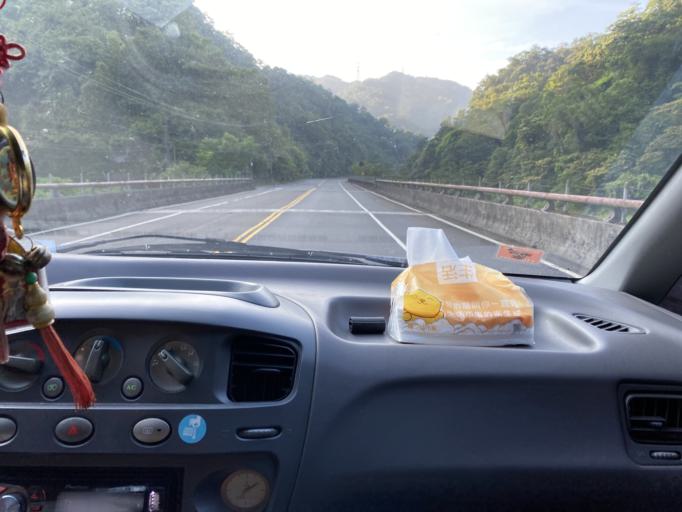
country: TW
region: Taiwan
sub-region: Keelung
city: Keelung
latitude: 25.0303
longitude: 121.7794
